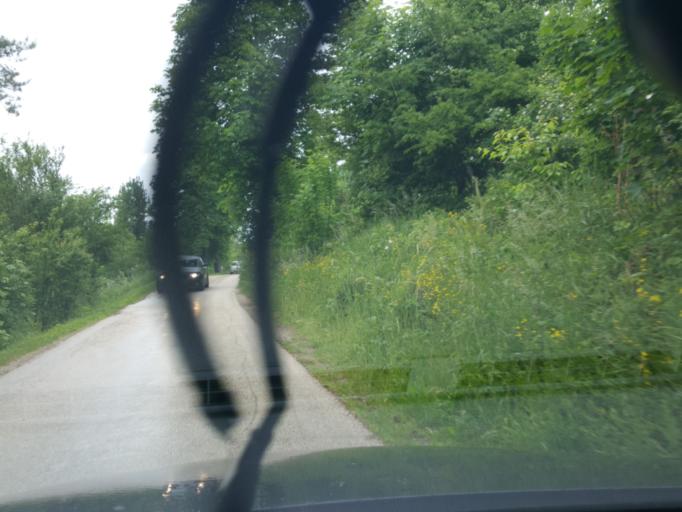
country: RS
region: Central Serbia
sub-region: Zajecarski Okrug
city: Boljevac
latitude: 43.7665
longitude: 21.9384
